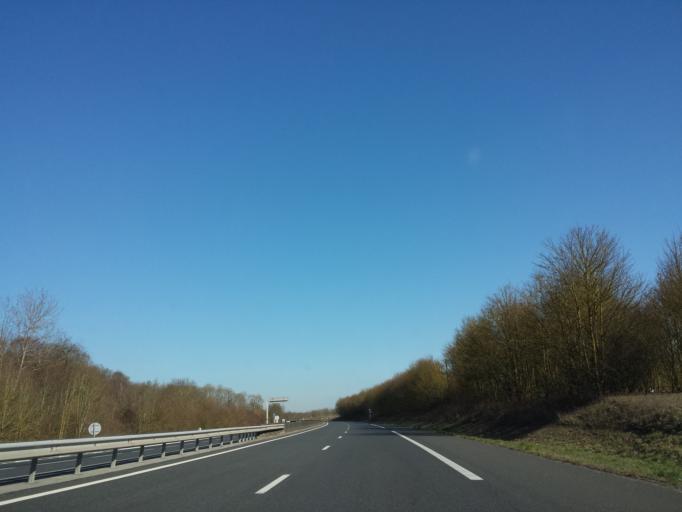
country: FR
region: Picardie
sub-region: Departement de l'Oise
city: Tille
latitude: 49.4653
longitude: 2.1607
